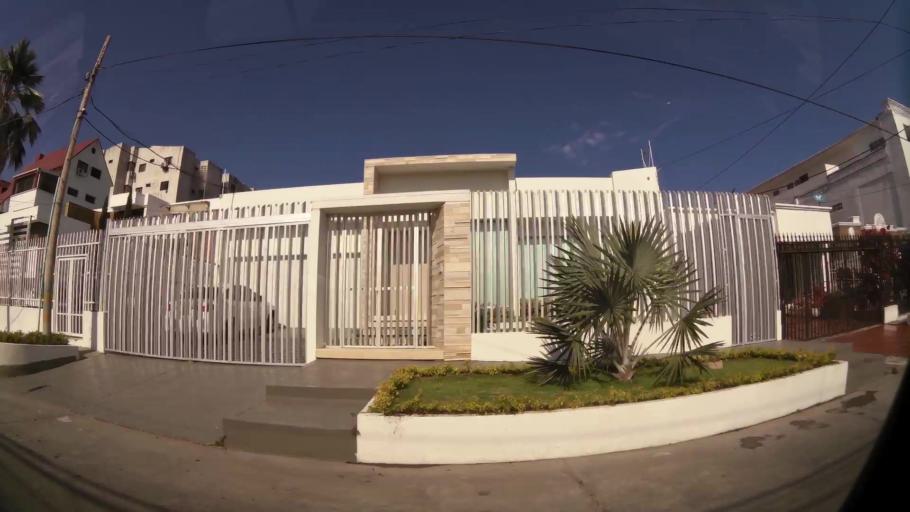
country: CO
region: Atlantico
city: Barranquilla
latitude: 11.0006
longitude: -74.8303
